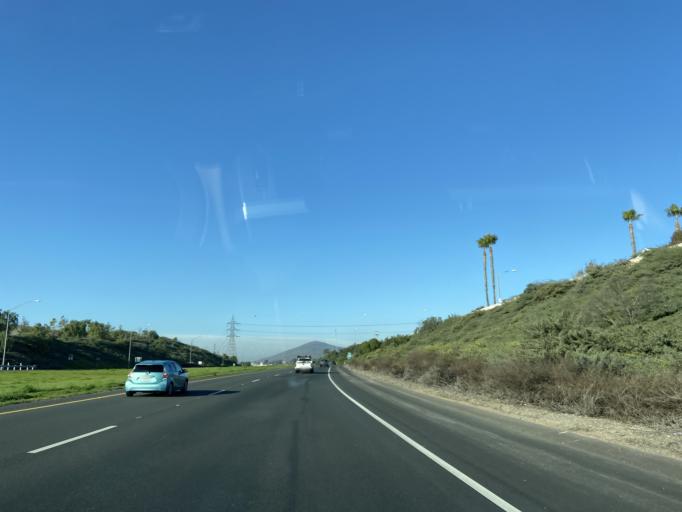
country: US
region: California
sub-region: San Diego County
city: Bonita
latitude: 32.6362
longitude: -116.9711
